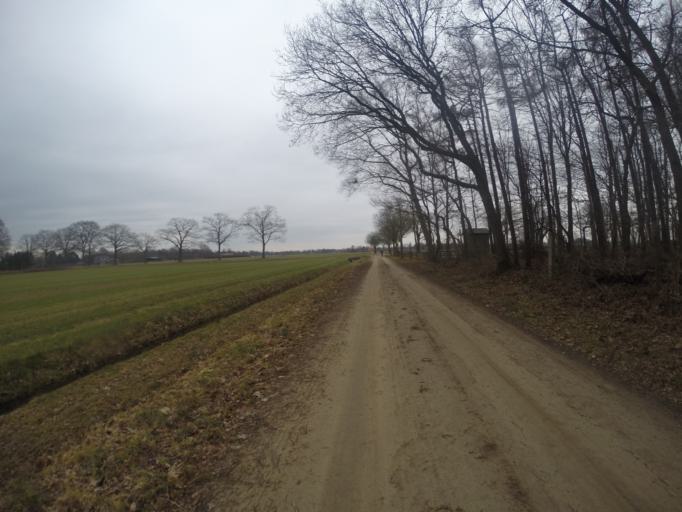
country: NL
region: Gelderland
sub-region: Gemeente Bronckhorst
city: Zelhem
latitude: 52.0307
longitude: 6.3454
